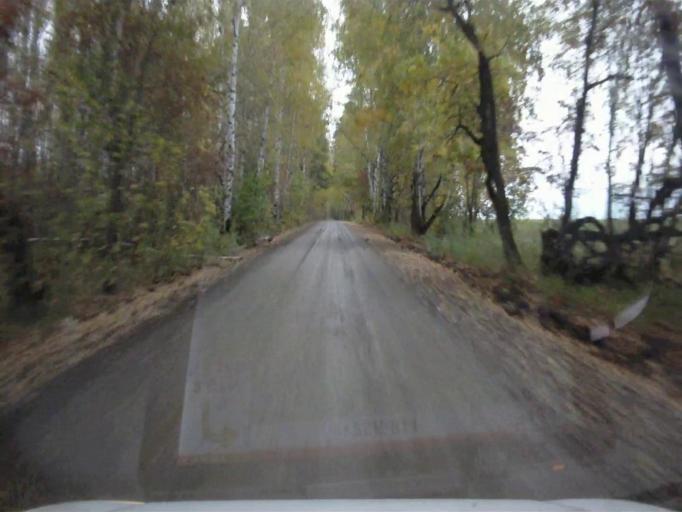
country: RU
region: Sverdlovsk
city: Mikhaylovsk
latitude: 56.1702
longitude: 59.2243
